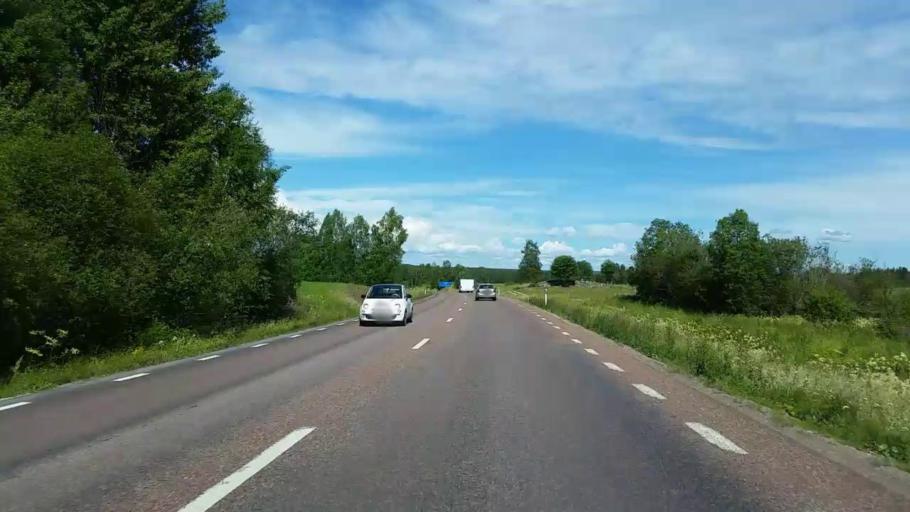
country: SE
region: Dalarna
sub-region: Rattviks Kommun
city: Raettvik
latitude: 60.9380
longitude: 15.2323
